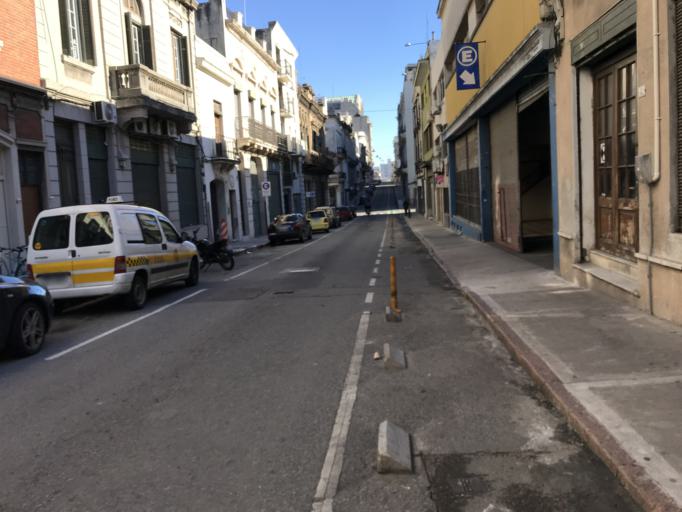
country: UY
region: Montevideo
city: Montevideo
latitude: -34.9040
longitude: -56.2057
